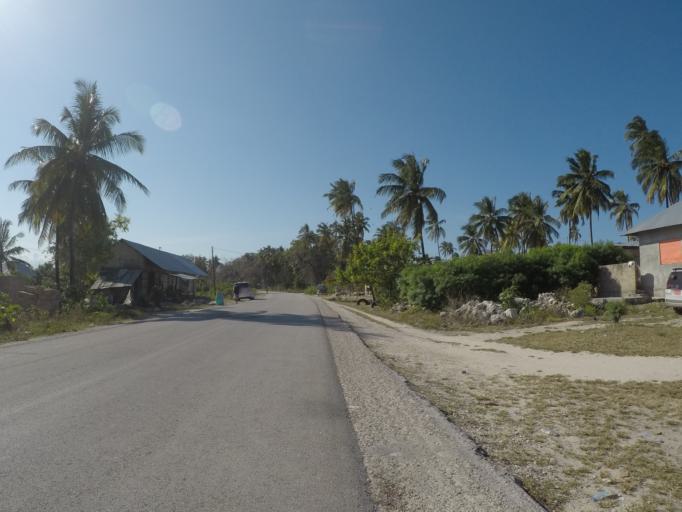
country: TZ
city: Kiwengwa
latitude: -6.1508
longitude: 39.5162
